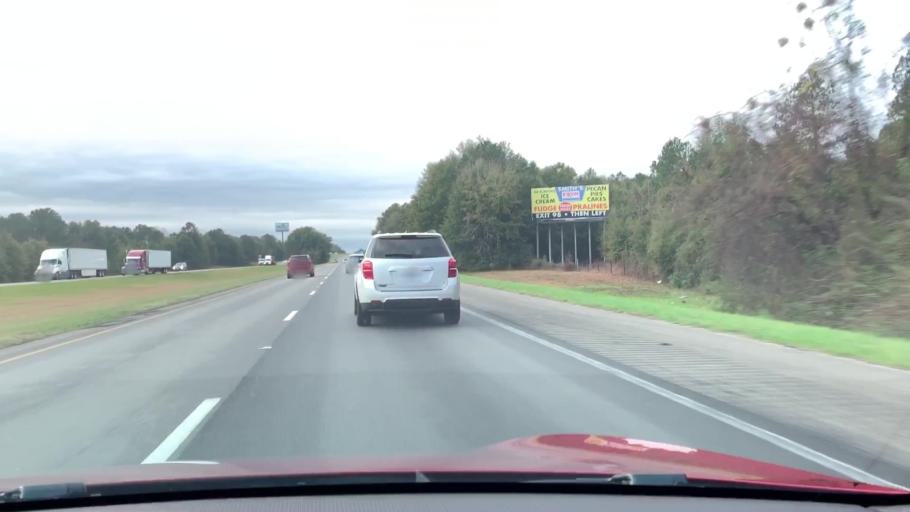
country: US
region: South Carolina
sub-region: Orangeburg County
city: Holly Hill
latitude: 33.5304
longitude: -80.4237
